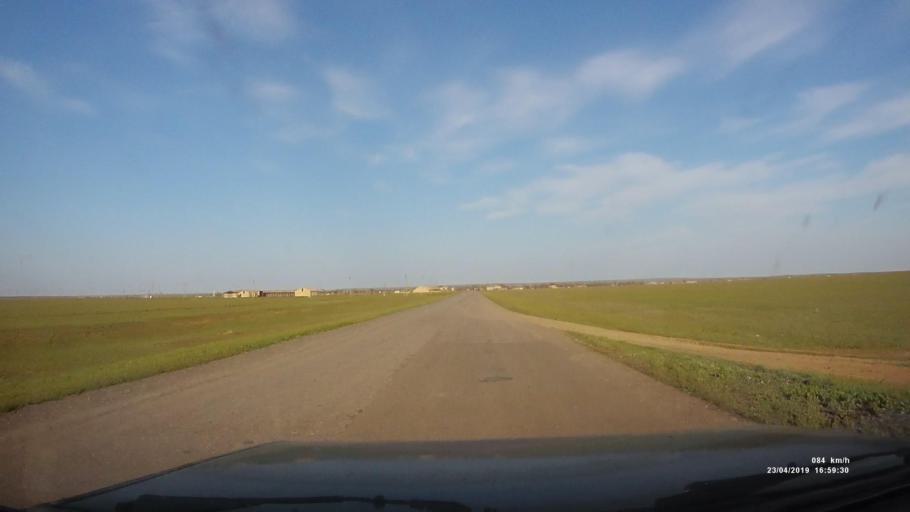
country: RU
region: Kalmykiya
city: Priyutnoye
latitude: 46.3083
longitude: 43.3914
